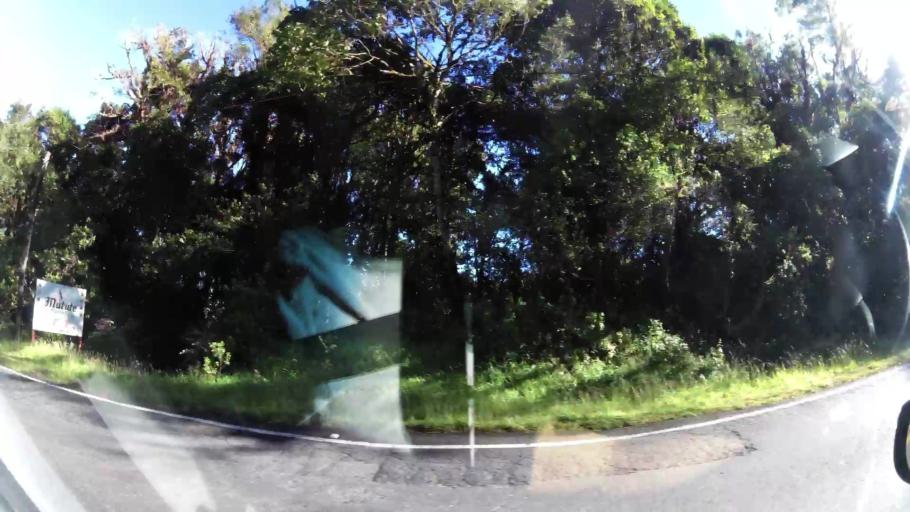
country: CR
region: San Jose
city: San Marcos
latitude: 9.7120
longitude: -83.9485
